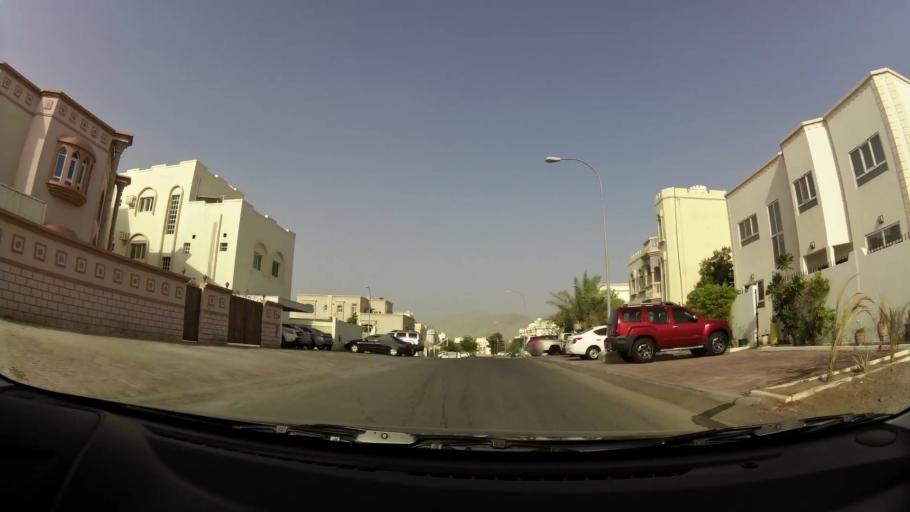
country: OM
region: Muhafazat Masqat
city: Bawshar
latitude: 23.5449
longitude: 58.3618
